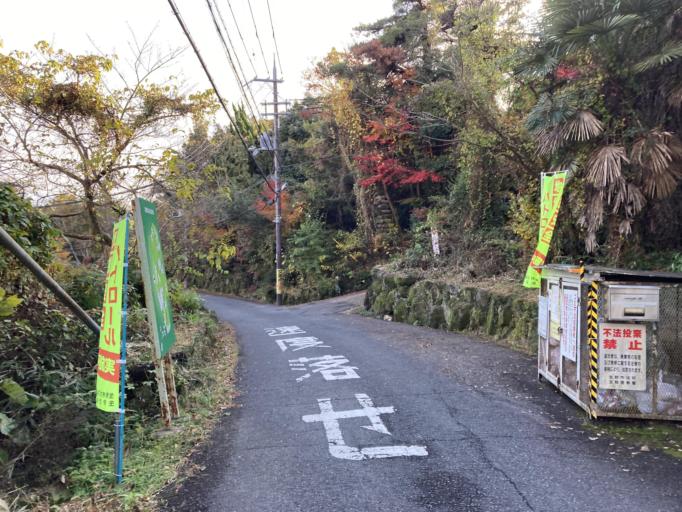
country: JP
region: Nara
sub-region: Ikoma-shi
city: Ikoma
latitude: 34.6761
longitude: 135.6905
